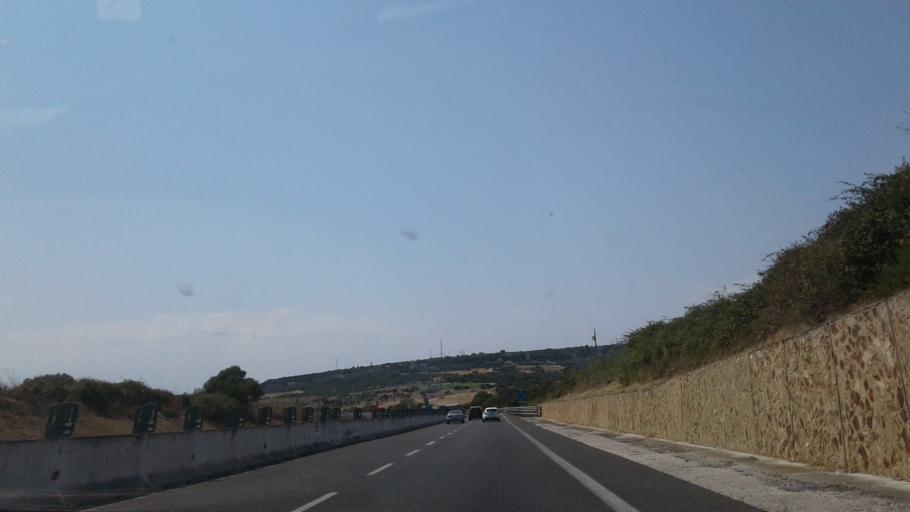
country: IT
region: Sardinia
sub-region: Provincia di Sassari
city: Sassari
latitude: 40.7140
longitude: 8.5345
